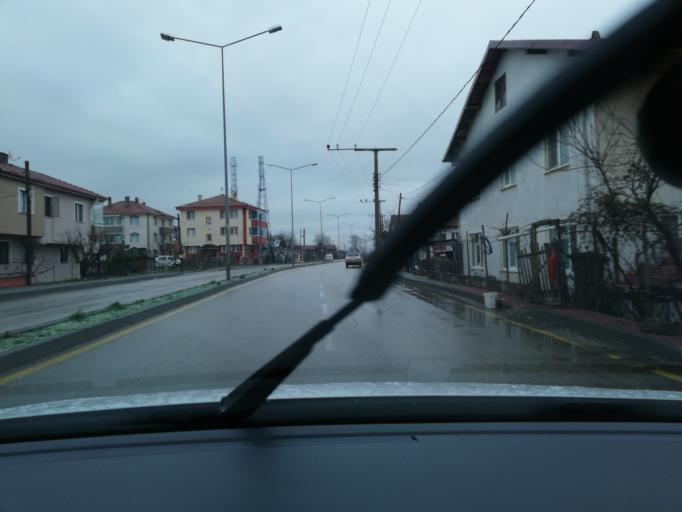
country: TR
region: Bolu
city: Bolu
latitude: 40.7233
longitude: 31.6150
